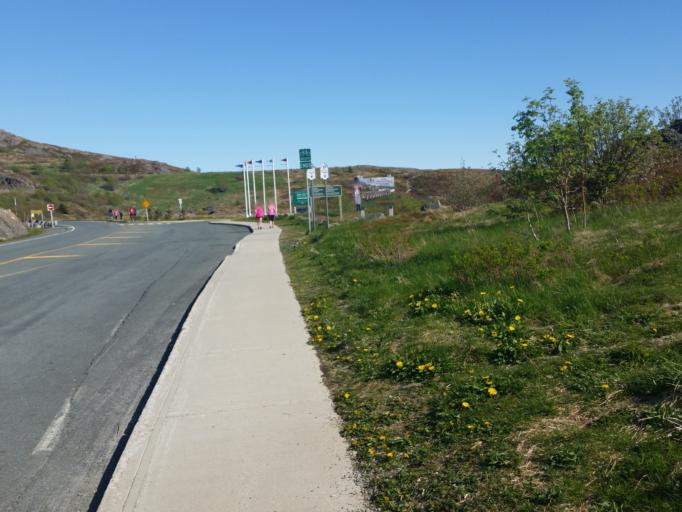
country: CA
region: Newfoundland and Labrador
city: St. John's
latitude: 47.5719
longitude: -52.6877
